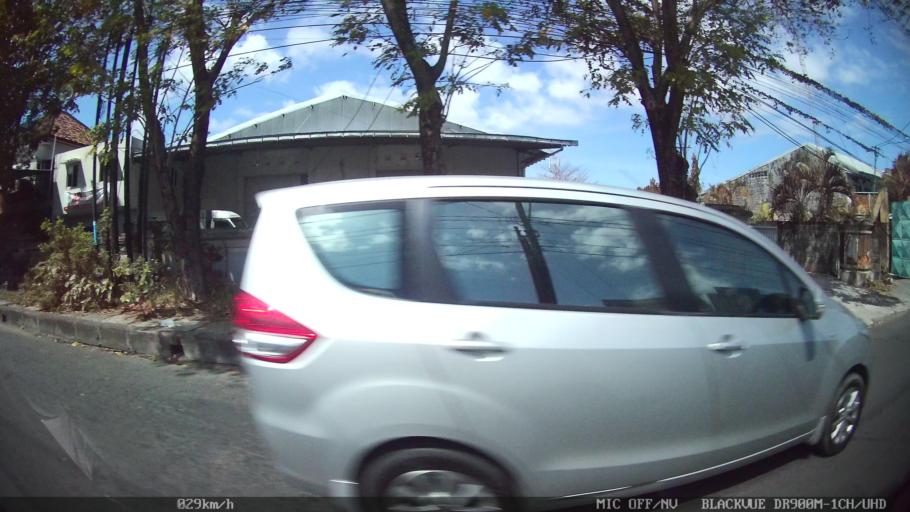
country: ID
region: Bali
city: Banjar Kertasari
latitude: -8.6429
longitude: 115.1856
